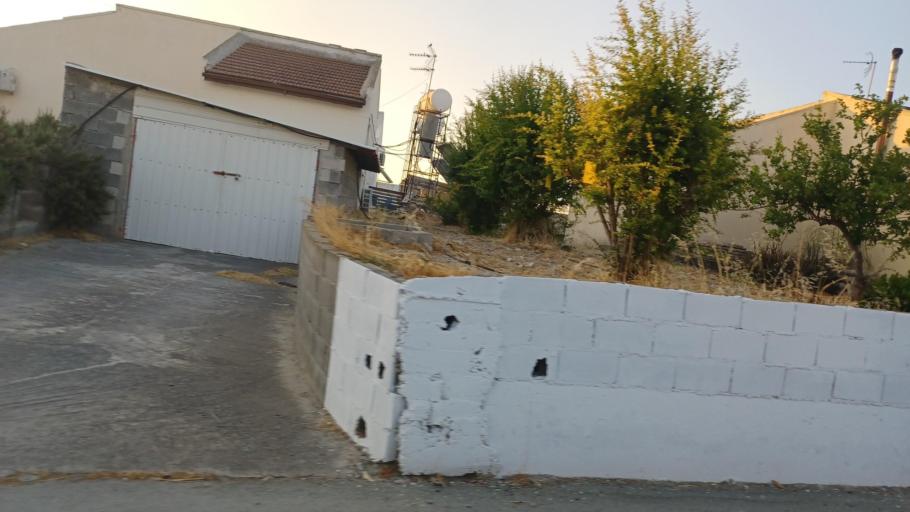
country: CY
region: Larnaka
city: Tersefanou
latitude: 34.8942
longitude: 33.5143
